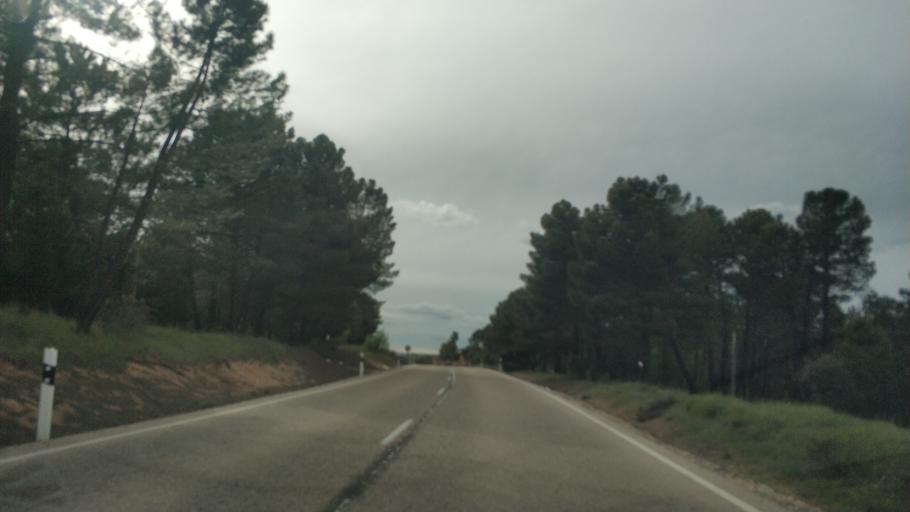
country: ES
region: Castille and Leon
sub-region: Provincia de Soria
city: Valdenebro
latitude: 41.5579
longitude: -2.9686
